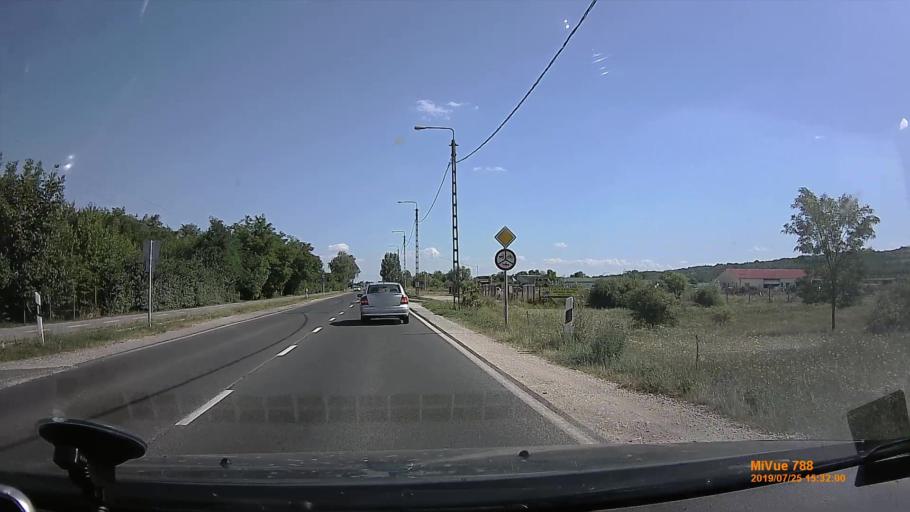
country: HU
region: Borsod-Abauj-Zemplen
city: Malyi
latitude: 48.0097
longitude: 20.8264
